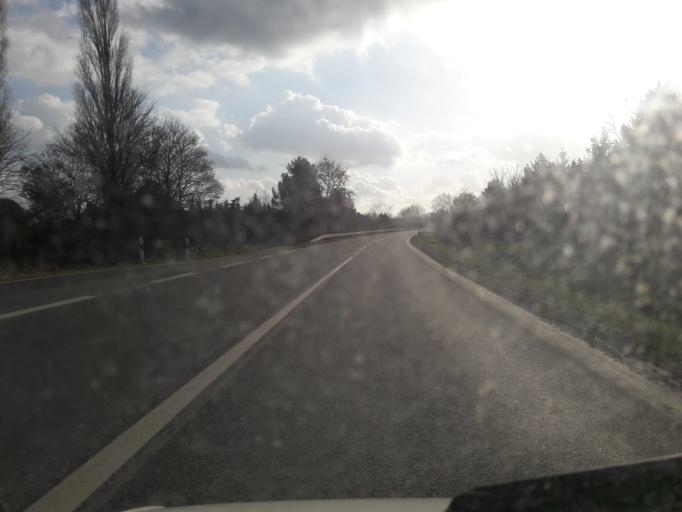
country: DE
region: Lower Saxony
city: Uchte
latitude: 52.5070
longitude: 8.9029
